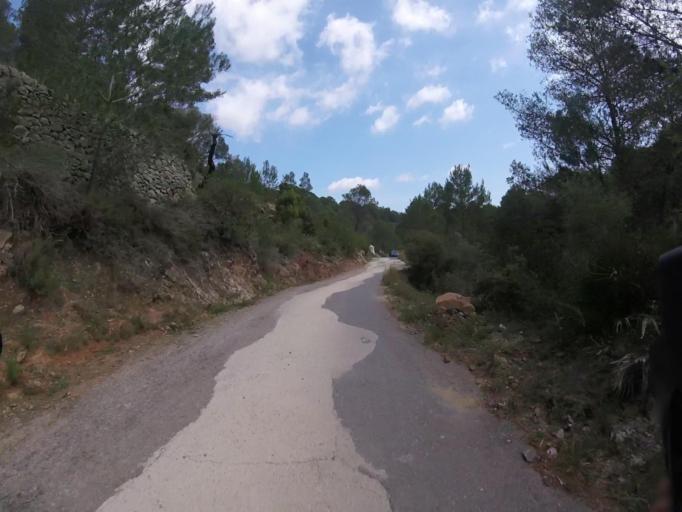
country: ES
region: Valencia
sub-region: Provincia de Castello
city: Cabanes
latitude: 40.1109
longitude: 0.0433
